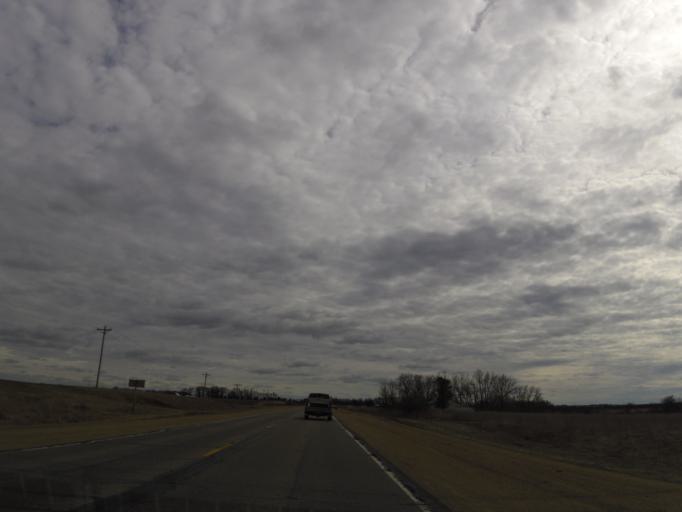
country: US
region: Iowa
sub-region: Howard County
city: Cresco
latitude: 43.2790
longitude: -92.2990
